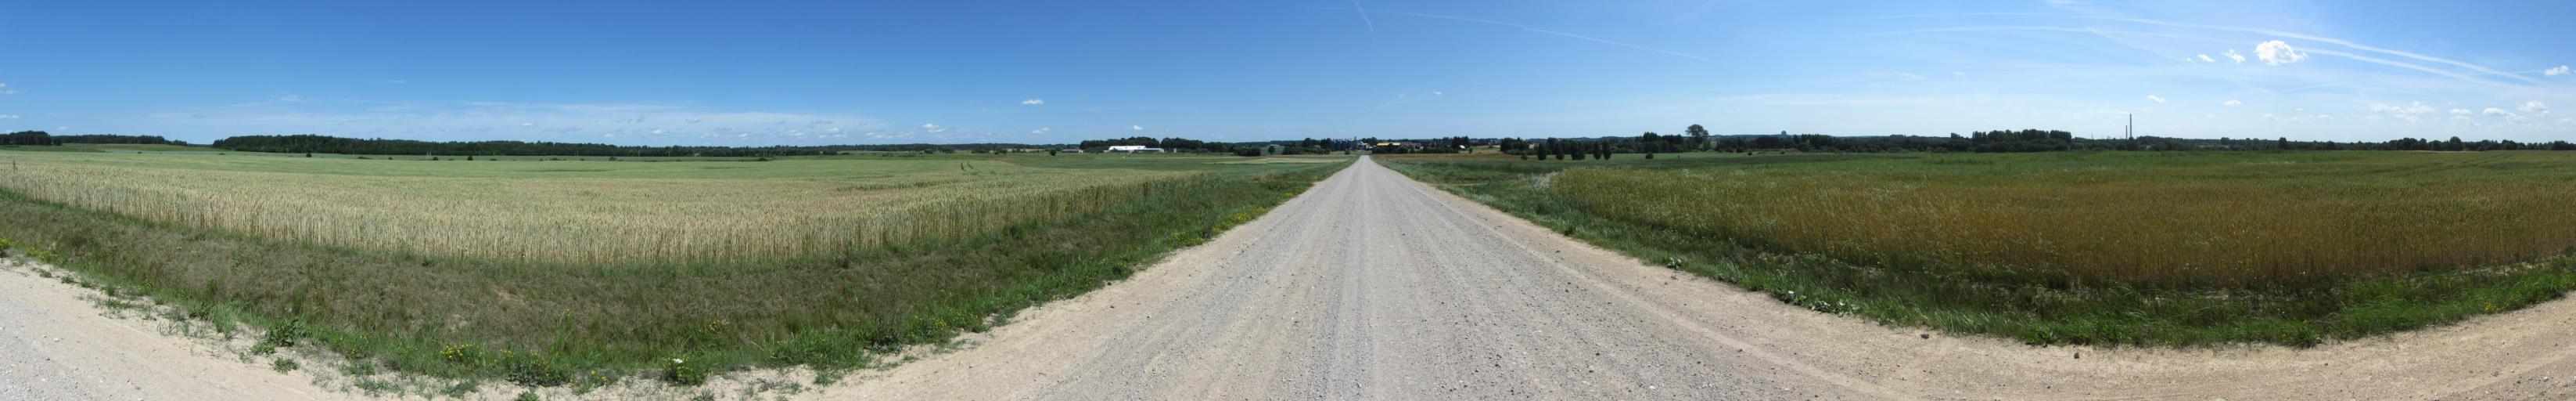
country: LT
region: Vilnius County
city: Elektrenai
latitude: 54.8089
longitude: 24.6336
